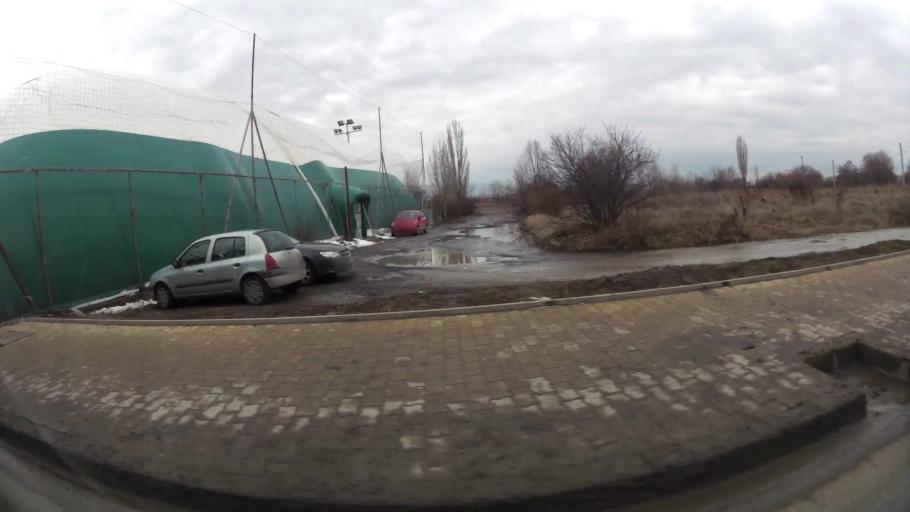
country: BG
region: Sofia-Capital
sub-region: Stolichna Obshtina
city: Sofia
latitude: 42.7410
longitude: 23.2864
